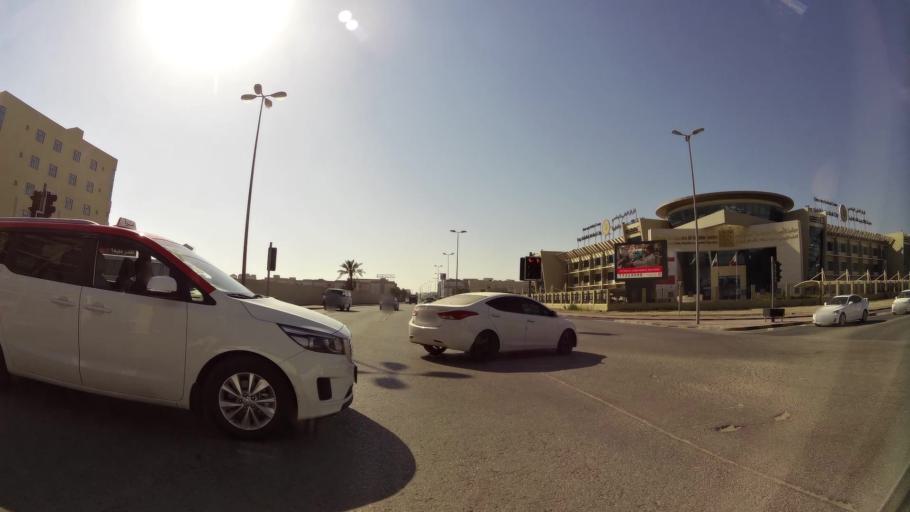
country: BH
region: Manama
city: Manama
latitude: 26.2123
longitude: 50.5757
